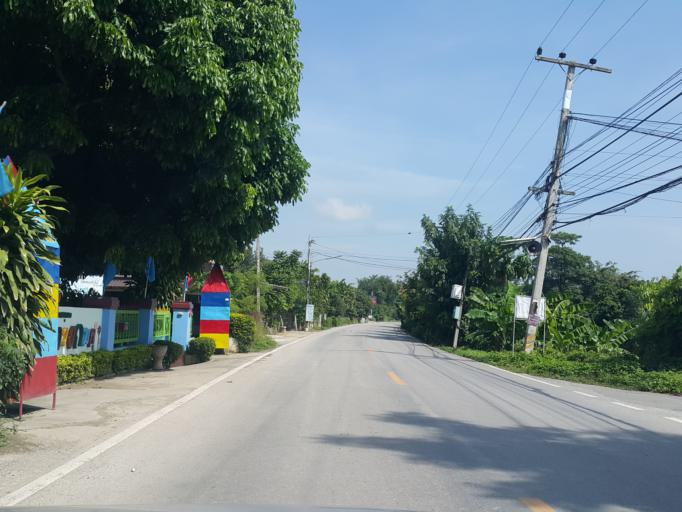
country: TH
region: Chiang Mai
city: Saraphi
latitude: 18.6855
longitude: 99.0612
